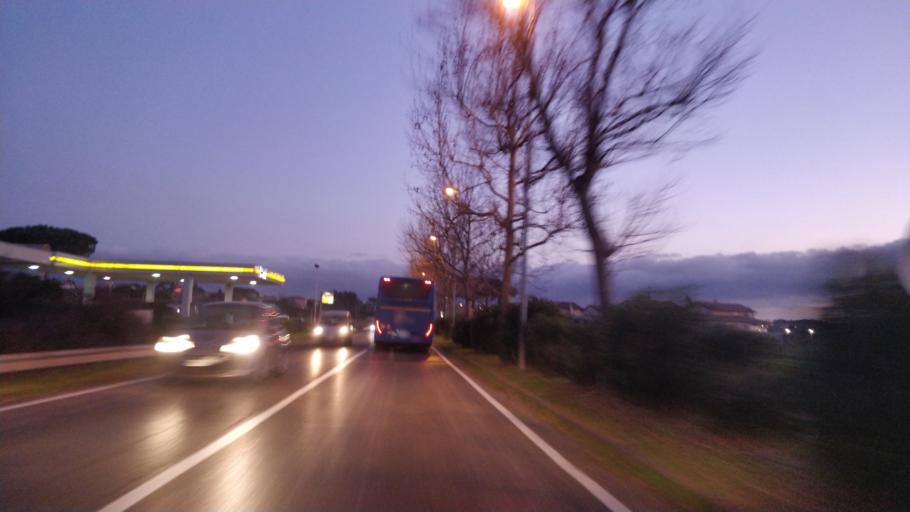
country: IT
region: Tuscany
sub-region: Provincia di Livorno
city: S.P. in Palazzi
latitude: 43.3202
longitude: 10.5118
